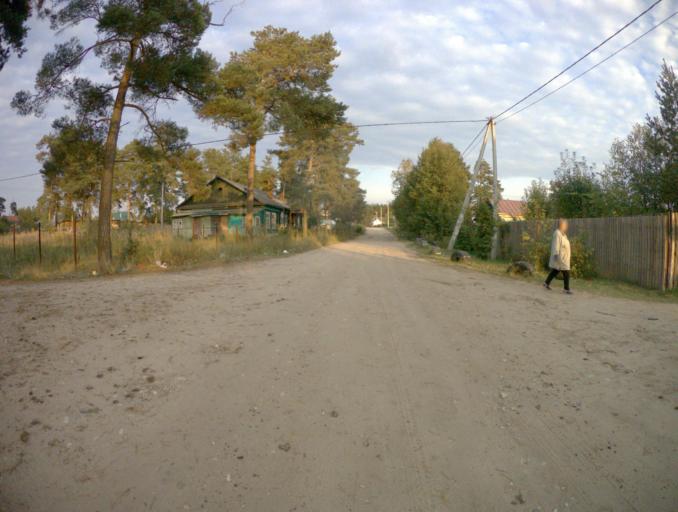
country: RU
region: Vladimir
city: Raduzhnyy
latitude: 56.0283
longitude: 40.3881
